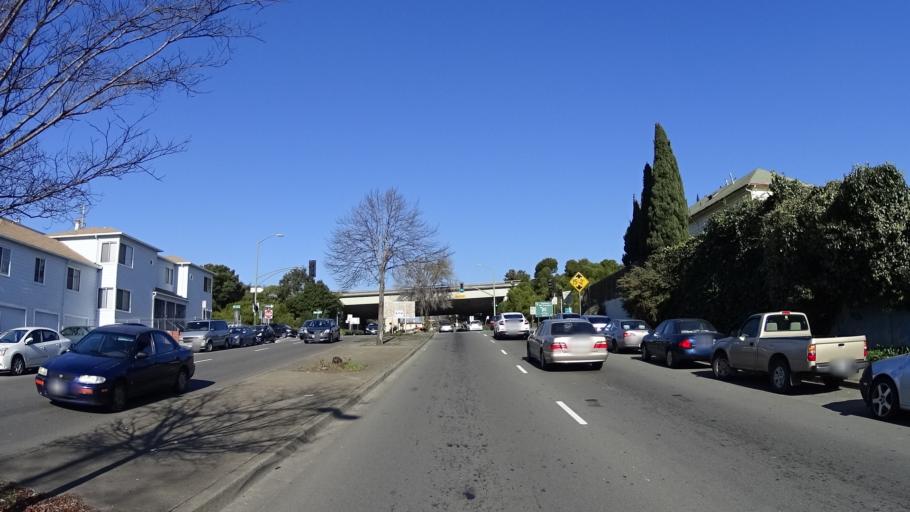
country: US
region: California
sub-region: Alameda County
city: Piedmont
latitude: 37.7999
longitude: -122.2291
